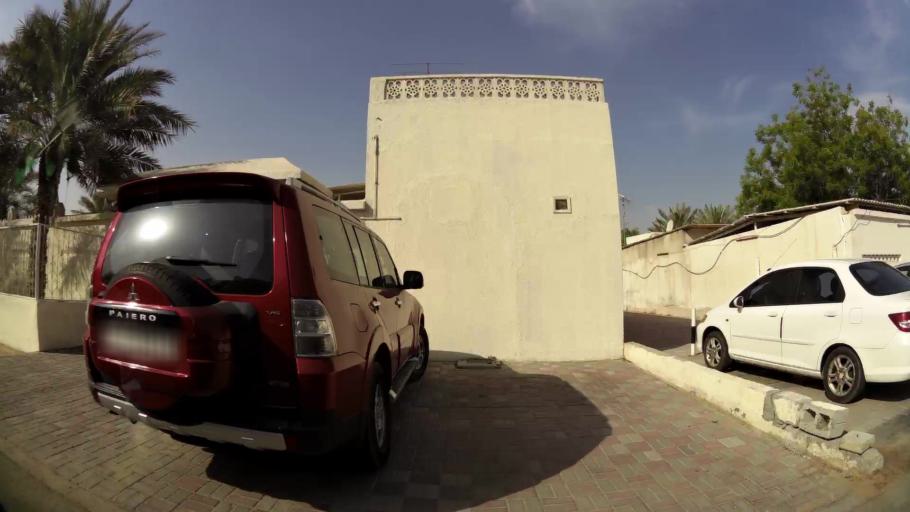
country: AE
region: Ash Shariqah
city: Sharjah
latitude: 25.2168
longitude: 55.3970
